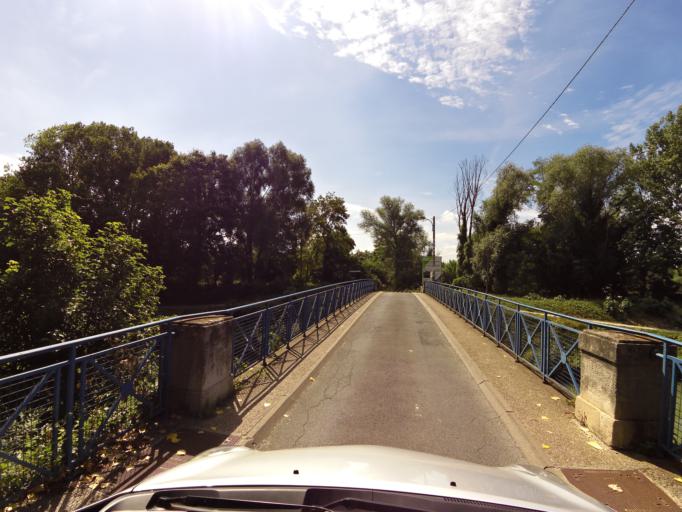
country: FR
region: Ile-de-France
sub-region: Departement de Seine-et-Marne
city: Chelles
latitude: 48.8684
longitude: 2.5979
